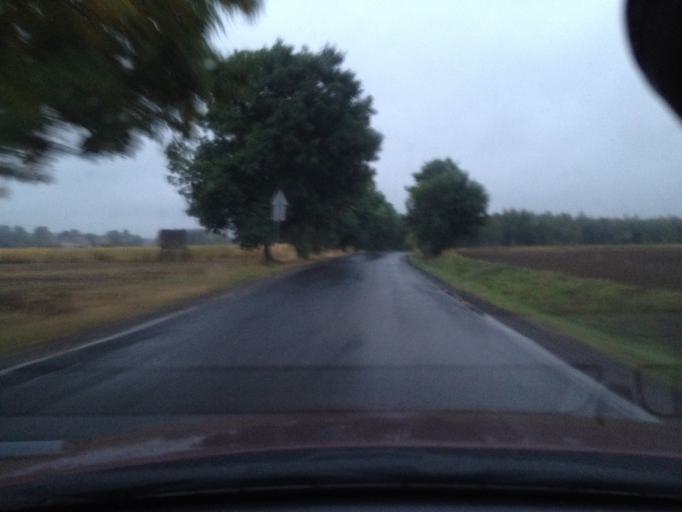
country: PL
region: Lower Silesian Voivodeship
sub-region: Powiat zgorzelecki
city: Lagow
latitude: 51.2017
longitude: 15.0658
